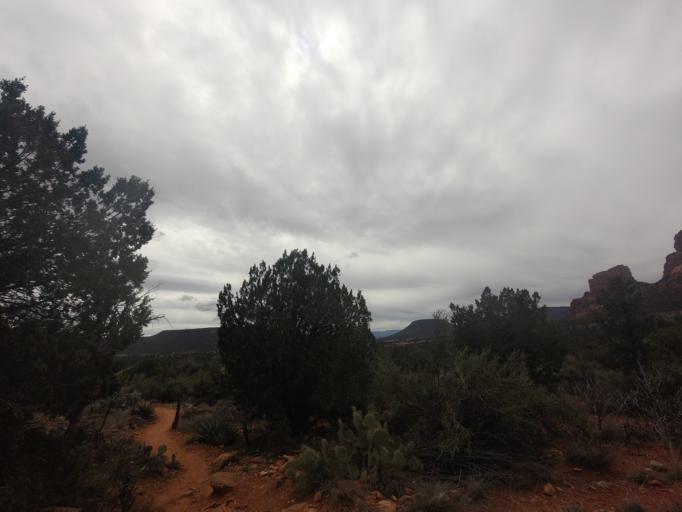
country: US
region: Arizona
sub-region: Yavapai County
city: Village of Oak Creek (Big Park)
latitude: 34.8002
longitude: -111.7603
